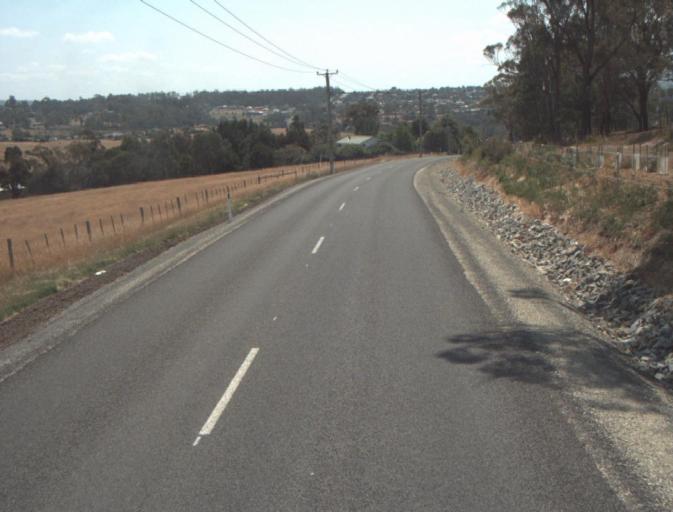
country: AU
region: Tasmania
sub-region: Launceston
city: Newstead
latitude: -41.4825
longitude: 147.1920
